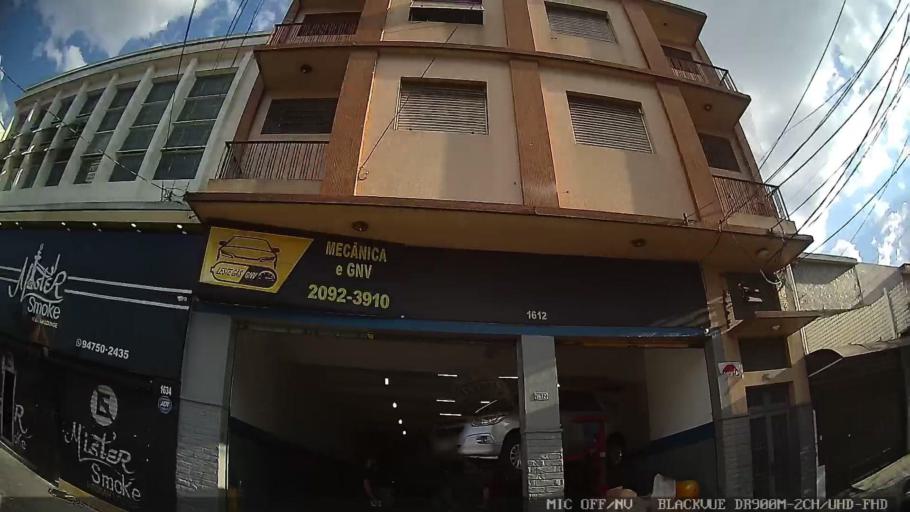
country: BR
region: Sao Paulo
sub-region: Sao Paulo
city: Sao Paulo
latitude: -23.5433
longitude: -46.5598
